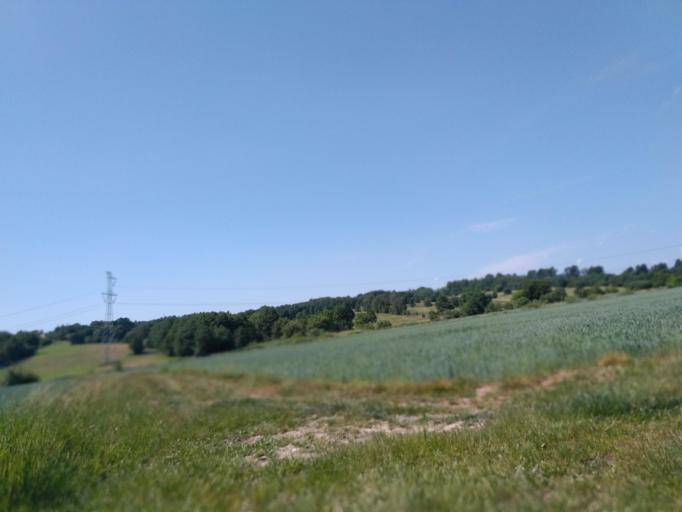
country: PL
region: Subcarpathian Voivodeship
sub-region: Krosno
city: Krosno
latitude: 49.7165
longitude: 21.7767
